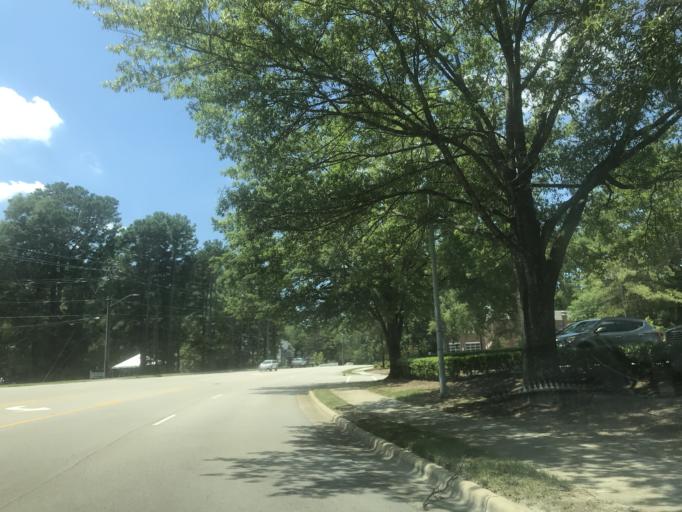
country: US
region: North Carolina
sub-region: Wake County
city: Cary
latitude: 35.7756
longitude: -78.7679
